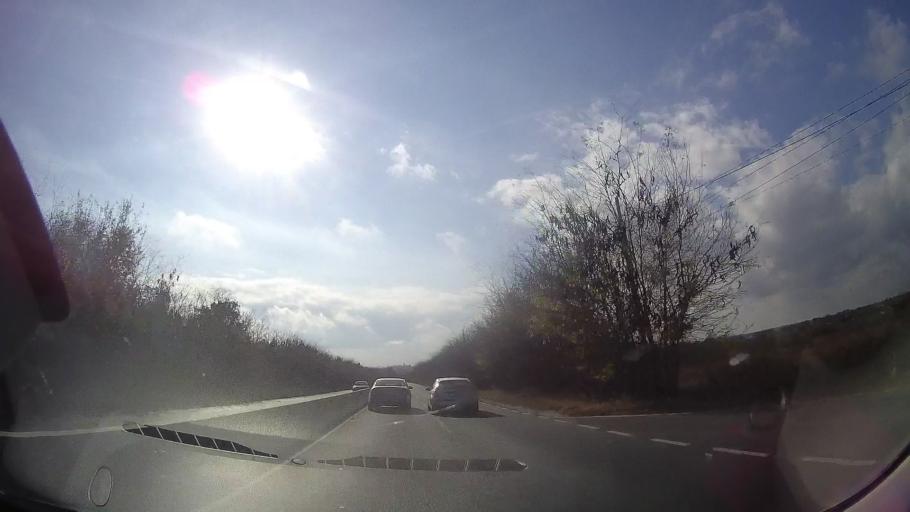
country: RO
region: Constanta
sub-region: Comuna Agigea
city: Agigea
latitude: 44.1235
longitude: 28.6135
